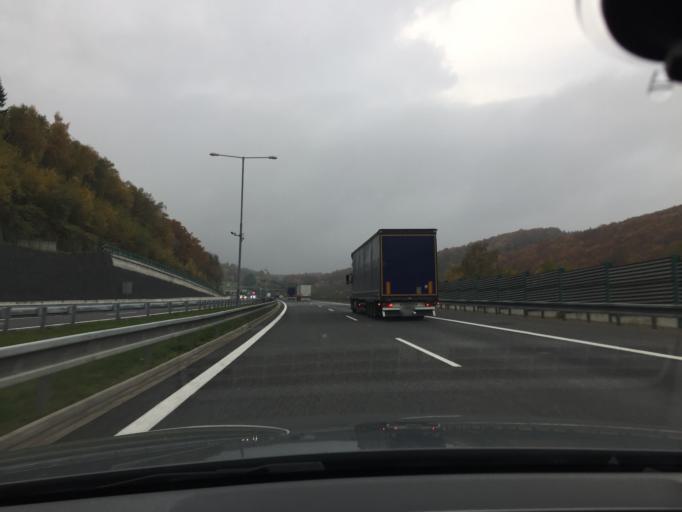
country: CZ
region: Ustecky
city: Libouchec
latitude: 50.7484
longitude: 14.0028
